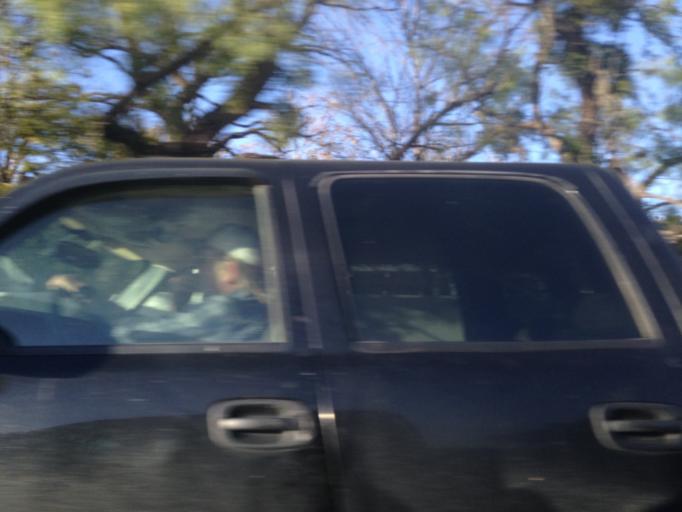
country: US
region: Texas
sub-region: Taylor County
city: Abilene
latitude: 32.4324
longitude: -99.7675
